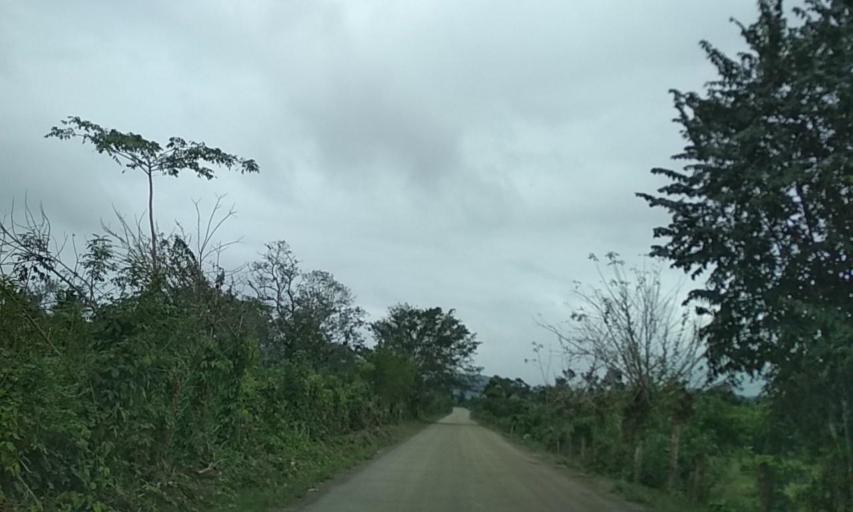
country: MX
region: Veracruz
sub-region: Papantla
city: El Chote
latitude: 20.3867
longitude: -97.3522
